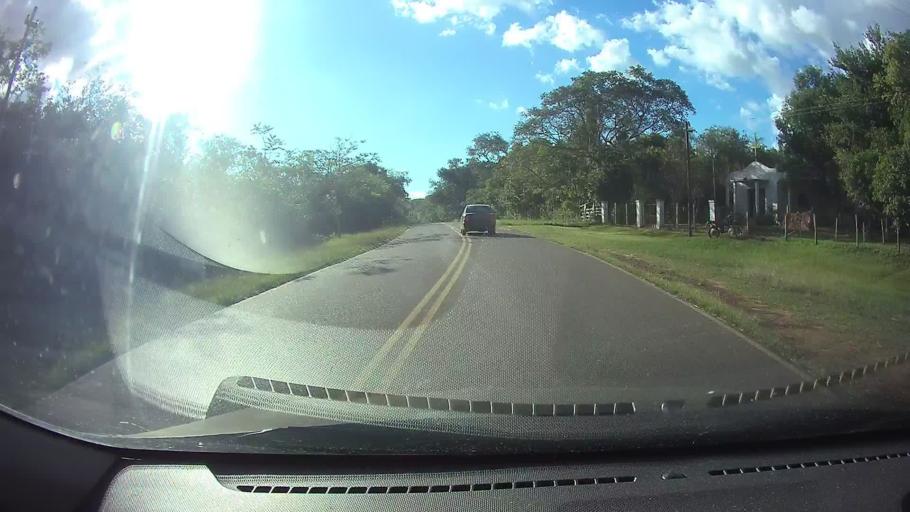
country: PY
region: Cordillera
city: Altos
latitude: -25.2799
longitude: -57.2133
